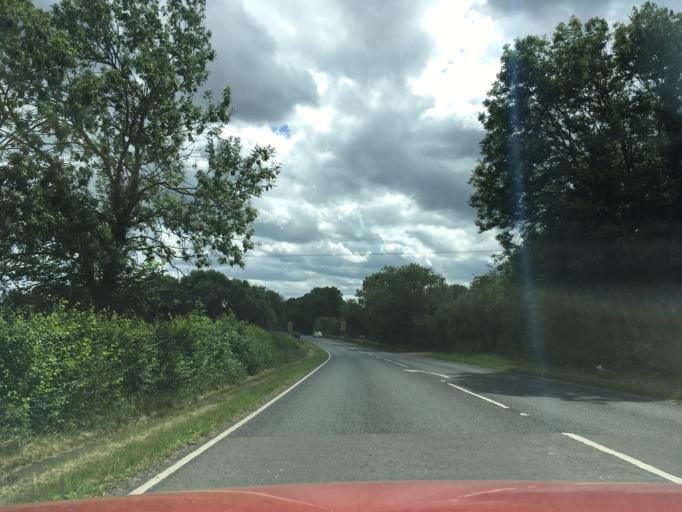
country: GB
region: England
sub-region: Nottinghamshire
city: East Leake
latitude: 52.8356
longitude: -1.1451
